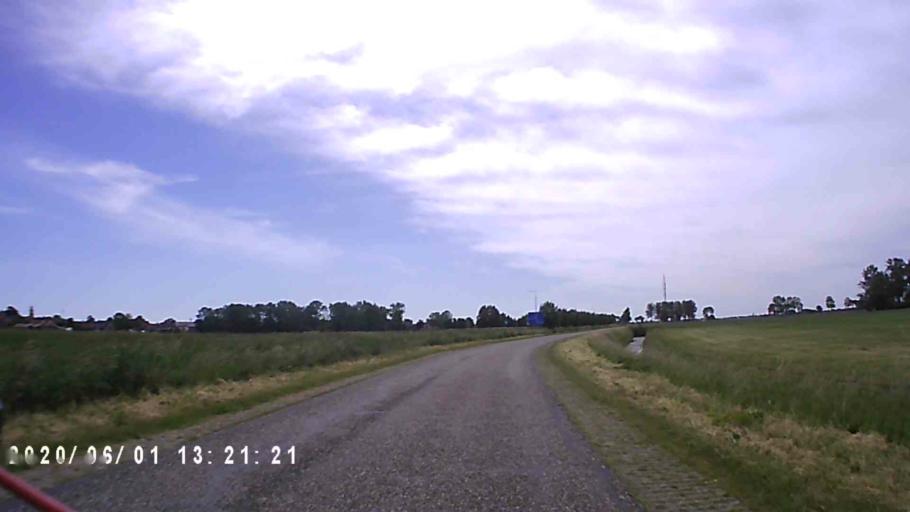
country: NL
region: Friesland
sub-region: Gemeente Littenseradiel
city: Wommels
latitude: 53.1122
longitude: 5.5836
